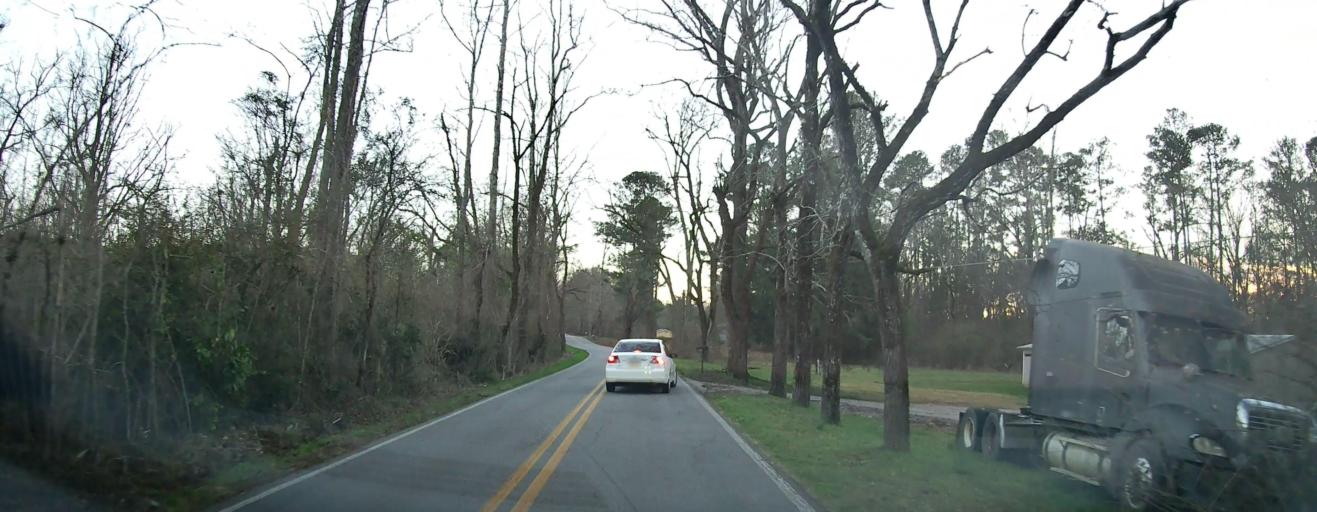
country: US
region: Georgia
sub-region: Troup County
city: La Grange
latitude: 33.0592
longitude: -84.9688
